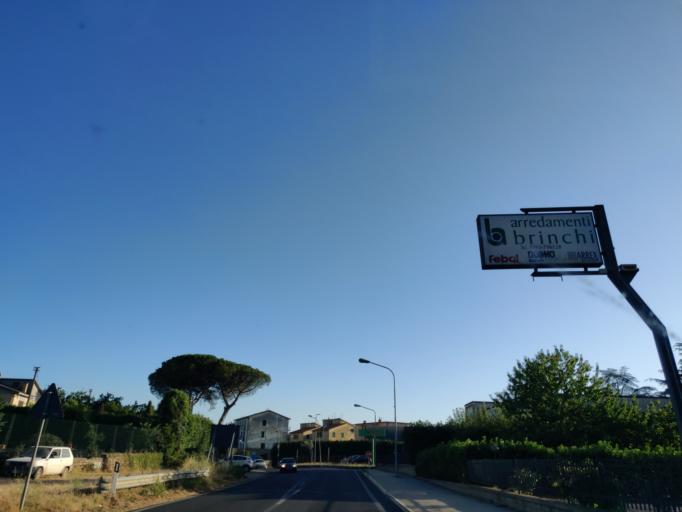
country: IT
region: Latium
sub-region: Provincia di Viterbo
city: Grotte di Castro
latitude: 42.6811
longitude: 11.8739
